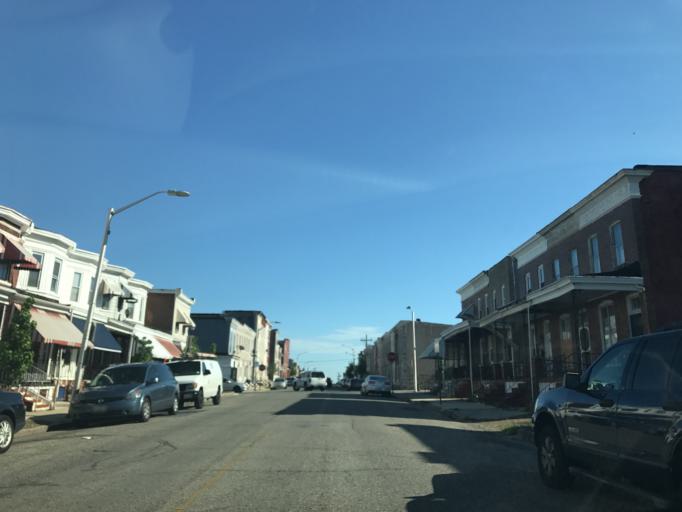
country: US
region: Maryland
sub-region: City of Baltimore
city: Baltimore
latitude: 39.3125
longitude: -76.6515
